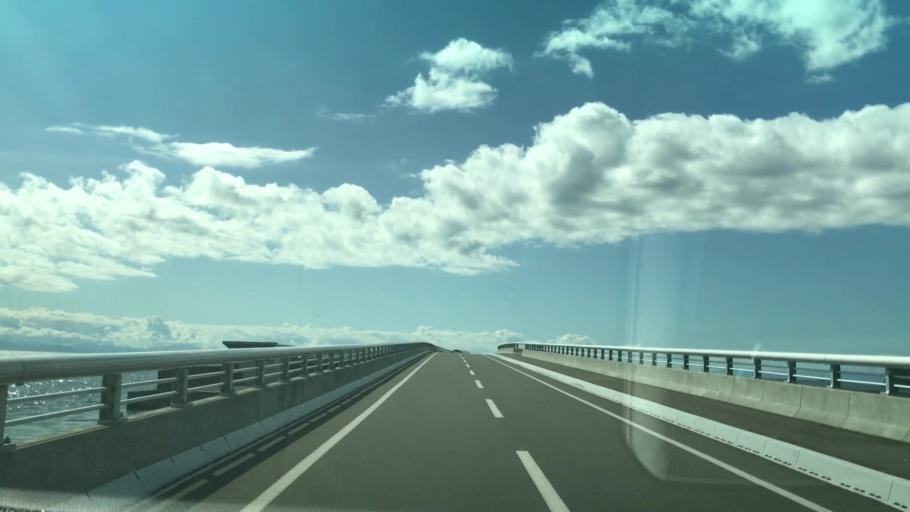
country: JP
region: Hokkaido
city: Muroran
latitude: 42.3097
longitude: 140.9644
